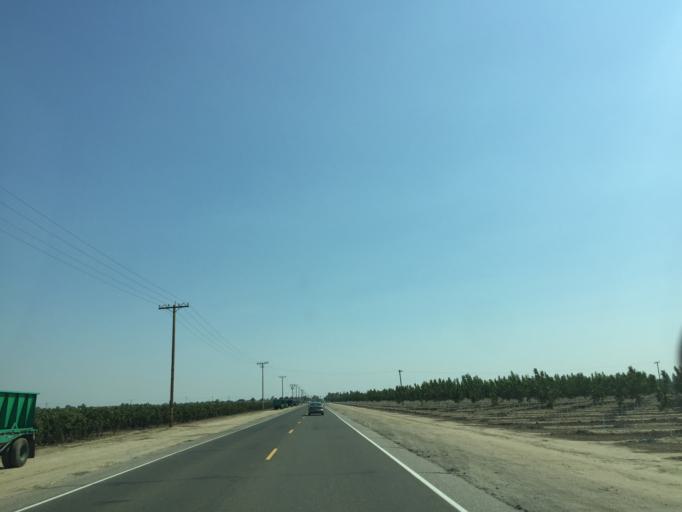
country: US
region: California
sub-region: Kings County
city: Lucerne
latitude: 36.3635
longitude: -119.6730
